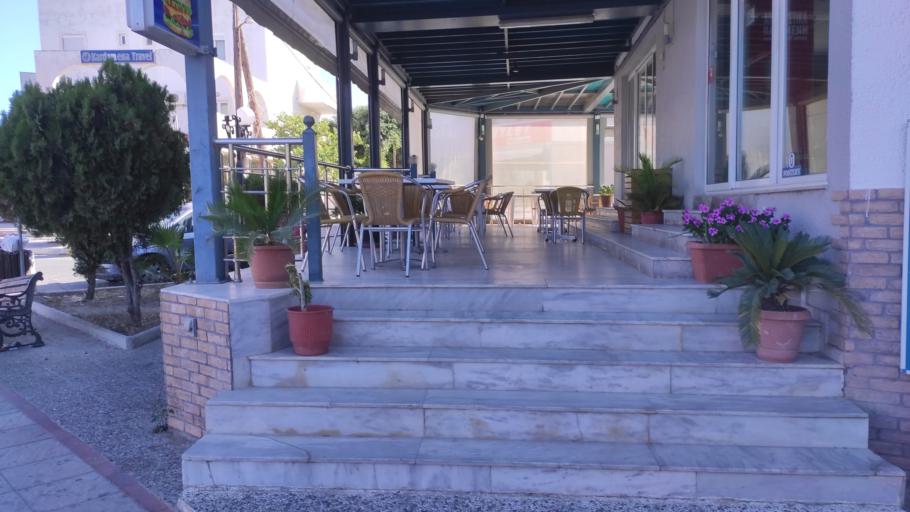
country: GR
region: South Aegean
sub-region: Nomos Dodekanisou
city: Kardamaina
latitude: 36.7829
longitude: 27.1429
